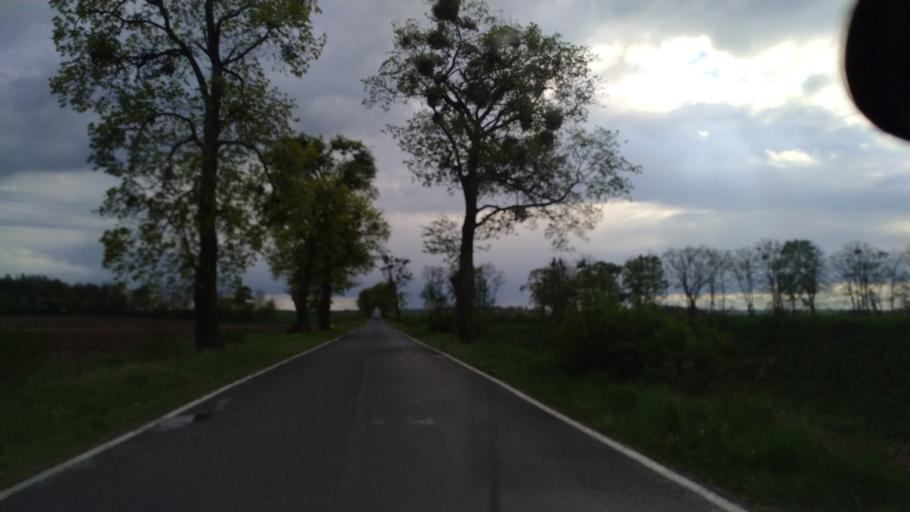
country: PL
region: Pomeranian Voivodeship
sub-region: Powiat starogardzki
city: Smetowo Graniczne
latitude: 53.7304
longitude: 18.6398
